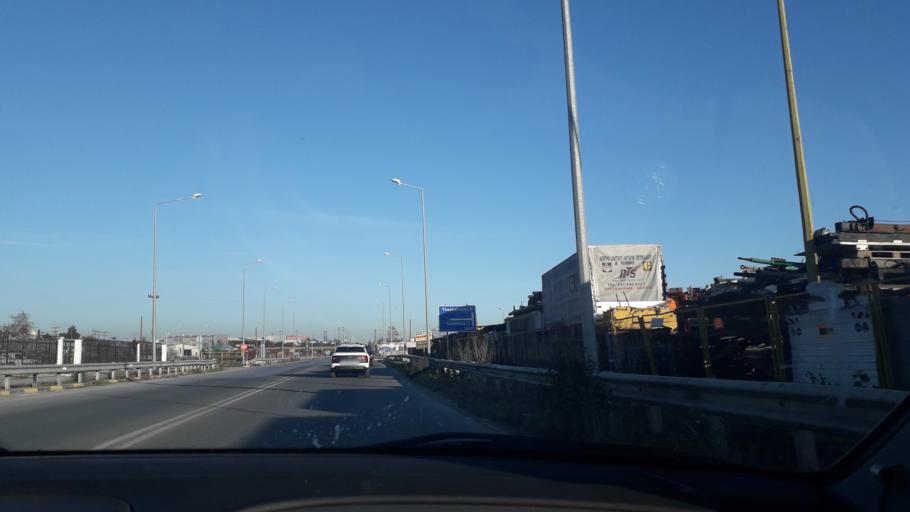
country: GR
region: Central Macedonia
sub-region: Nomos Pellis
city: Giannitsa
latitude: 40.7825
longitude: 22.3885
